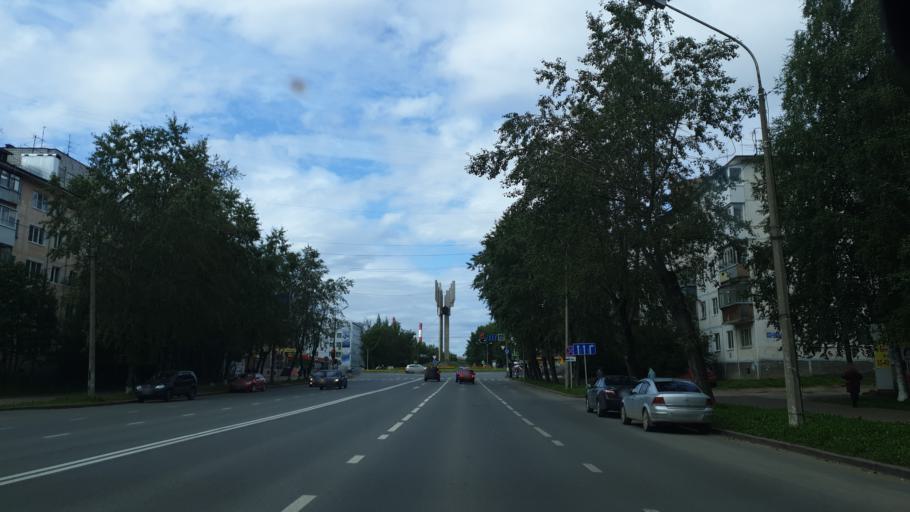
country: RU
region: Komi Republic
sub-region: Syktyvdinskiy Rayon
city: Syktyvkar
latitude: 61.6625
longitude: 50.8175
